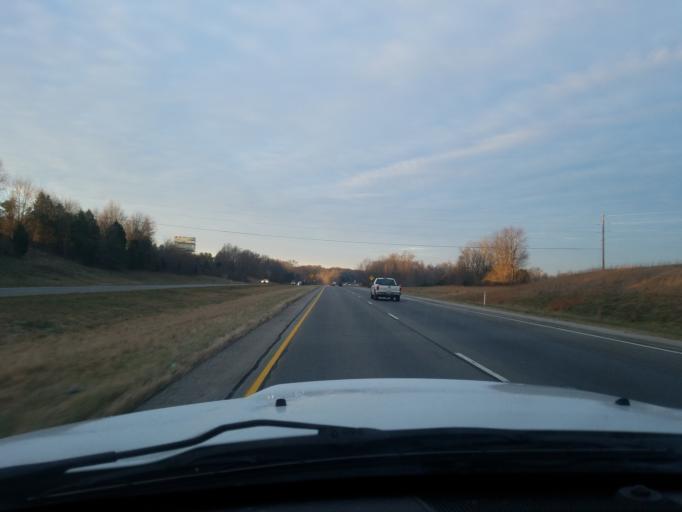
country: US
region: Indiana
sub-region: Floyd County
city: Georgetown
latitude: 38.2612
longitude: -86.0077
